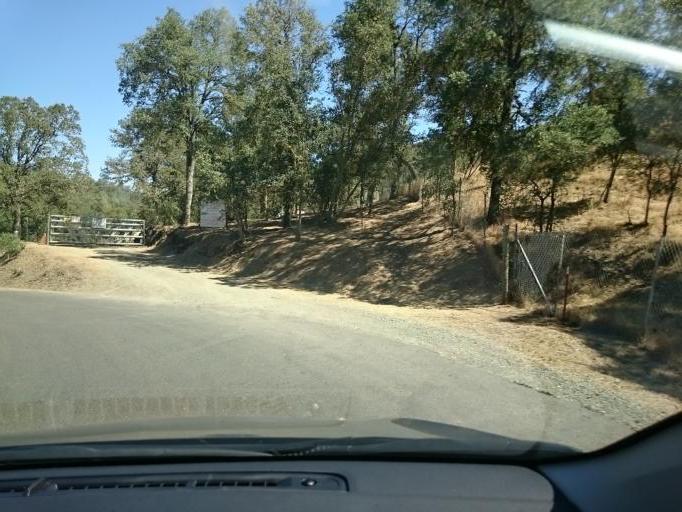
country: US
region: California
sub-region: Calaveras County
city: Rancho Calaveras
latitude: 38.1123
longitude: -120.7805
